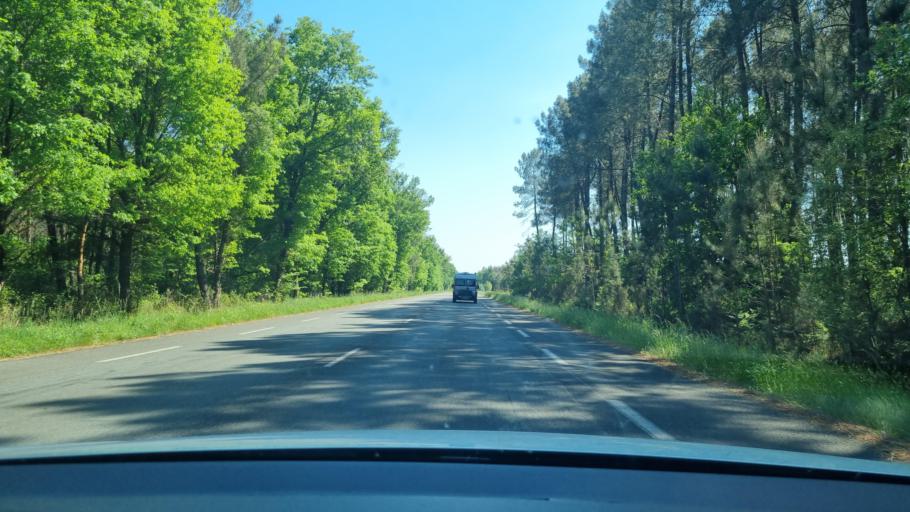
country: FR
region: Aquitaine
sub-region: Departement de la Gironde
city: Prechac
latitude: 44.2518
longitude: -0.2612
